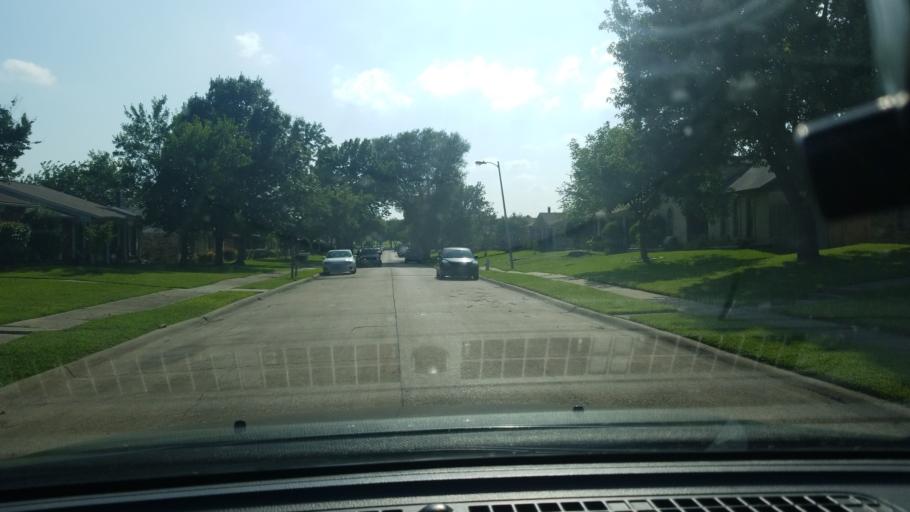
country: US
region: Texas
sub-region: Dallas County
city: Sunnyvale
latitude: 32.8183
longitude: -96.6043
